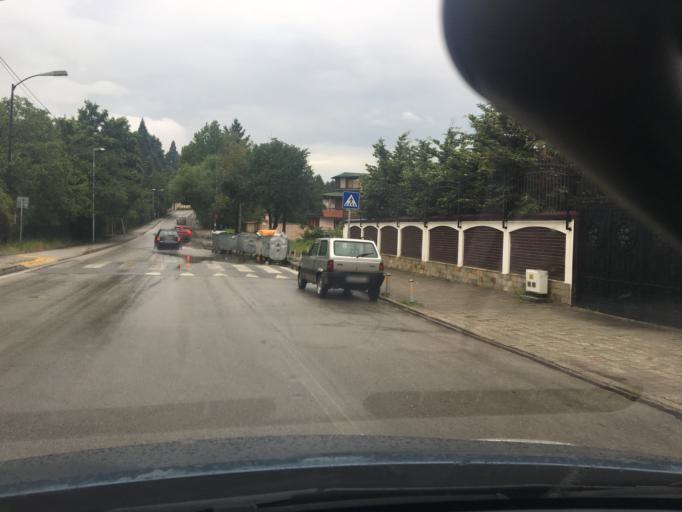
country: BG
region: Sofia-Capital
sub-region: Stolichna Obshtina
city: Sofia
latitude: 42.6430
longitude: 23.2824
